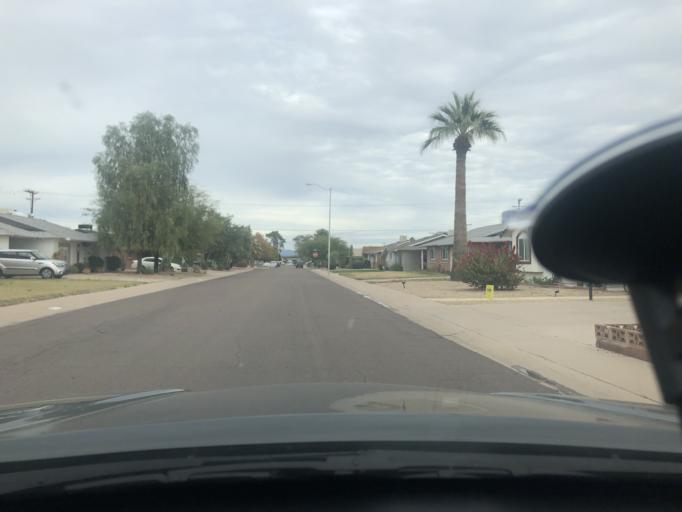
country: US
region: Arizona
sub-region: Maricopa County
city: Scottsdale
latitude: 33.4788
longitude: -111.8973
